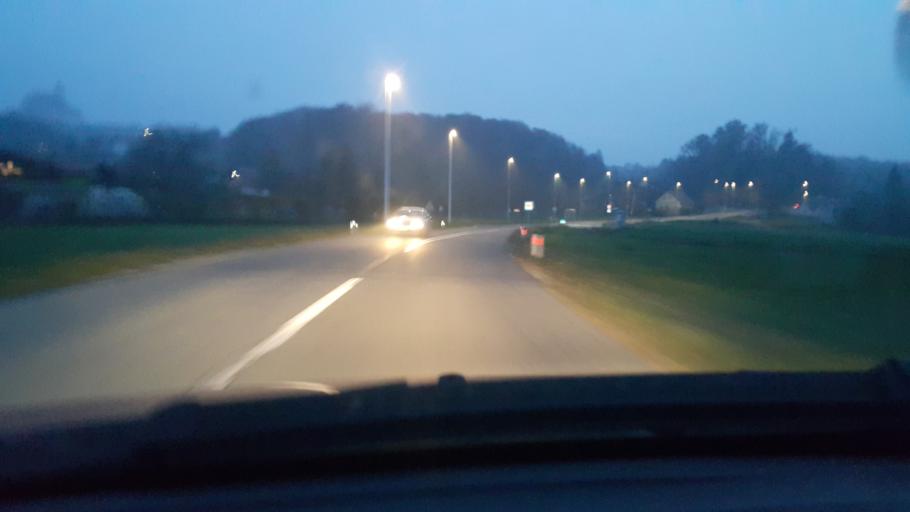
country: SI
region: Majsperk
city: Majsperk
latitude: 46.3619
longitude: 15.7610
